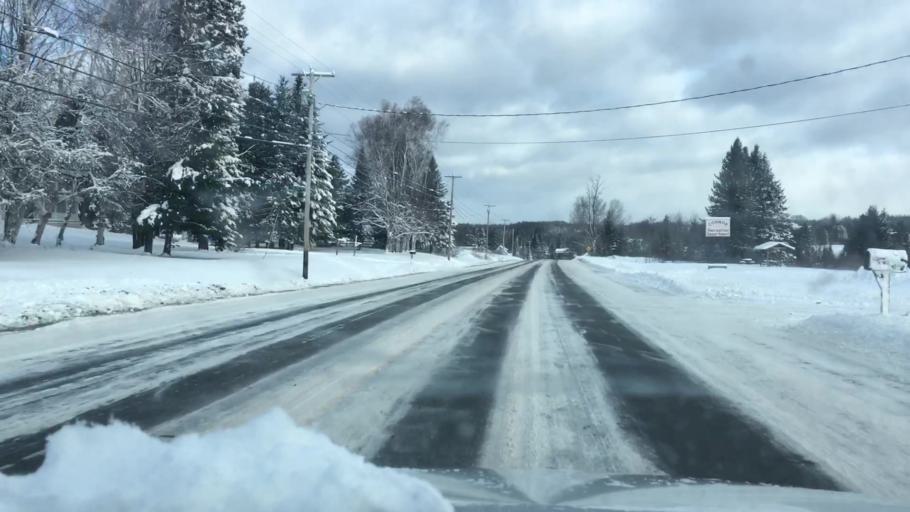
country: US
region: Maine
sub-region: Aroostook County
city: Caribou
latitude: 46.9732
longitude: -68.0358
